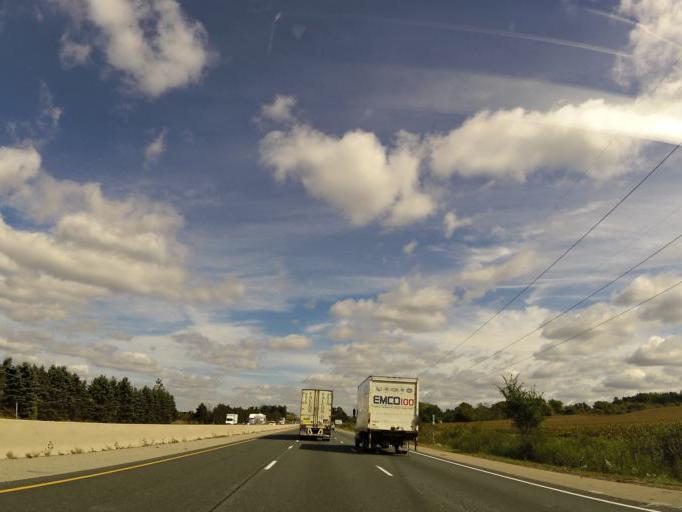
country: CA
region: Ontario
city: Dorchester
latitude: 42.9702
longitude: -80.9868
